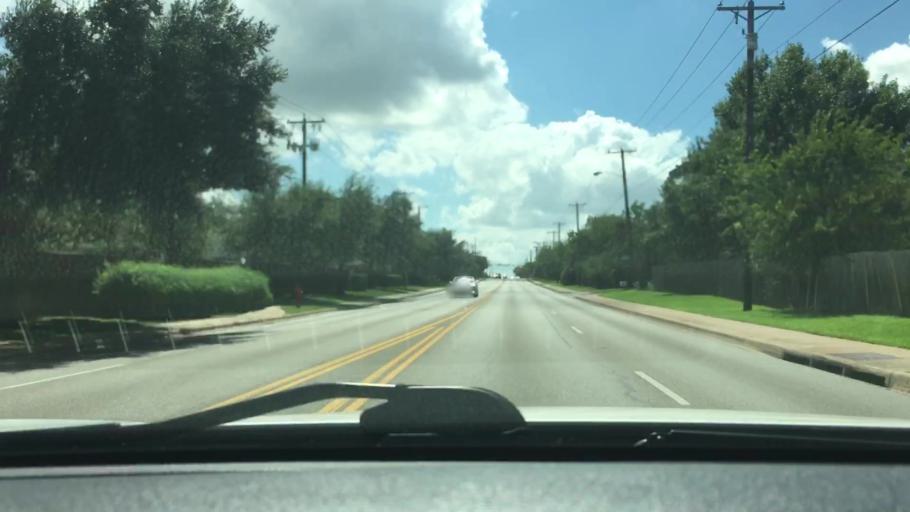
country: US
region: Texas
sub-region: Williamson County
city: Round Rock
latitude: 30.5340
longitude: -97.6680
